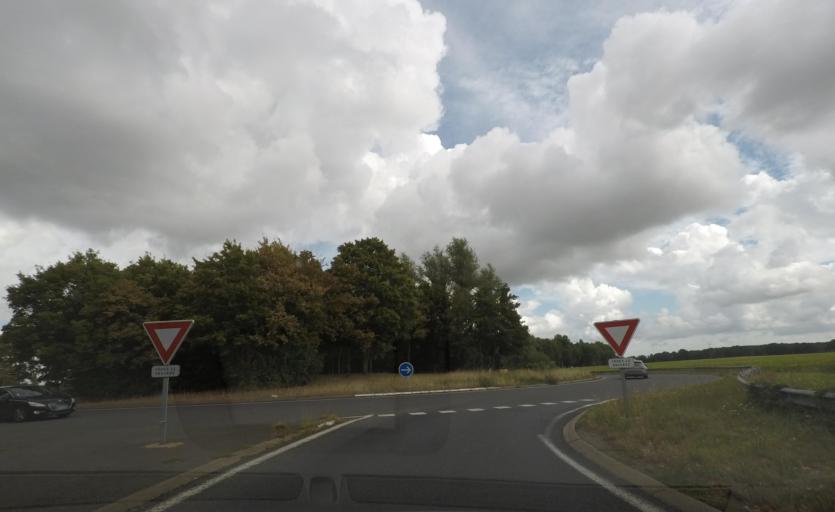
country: FR
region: Pays de la Loire
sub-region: Departement de Maine-et-Loire
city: Pellouailles-les-Vignes
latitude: 47.5249
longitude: -0.4276
